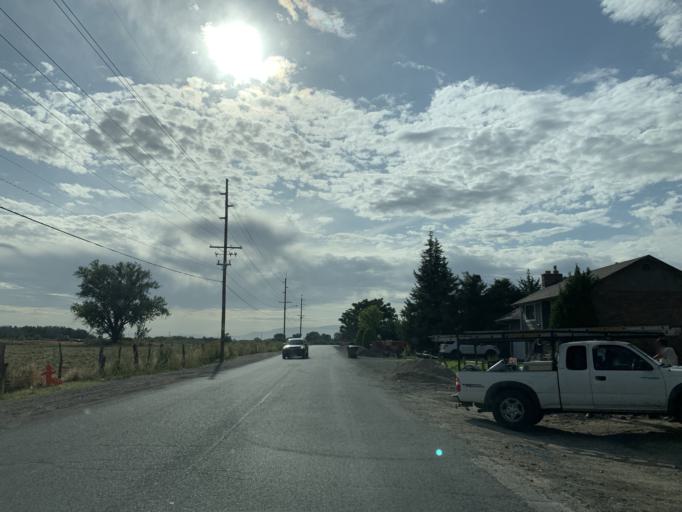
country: US
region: Utah
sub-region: Utah County
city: Provo
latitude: 40.2185
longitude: -111.6851
